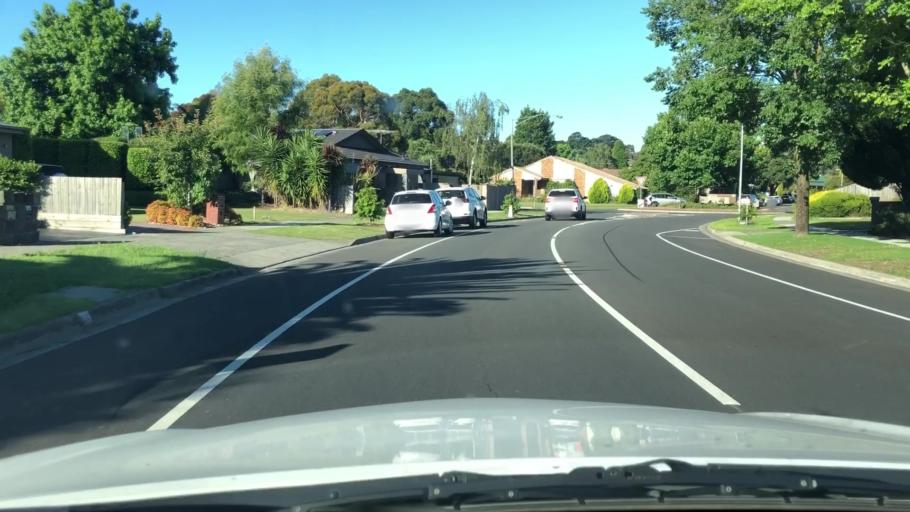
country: AU
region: Victoria
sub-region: Knox
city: Rowville
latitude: -37.9293
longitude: 145.2406
